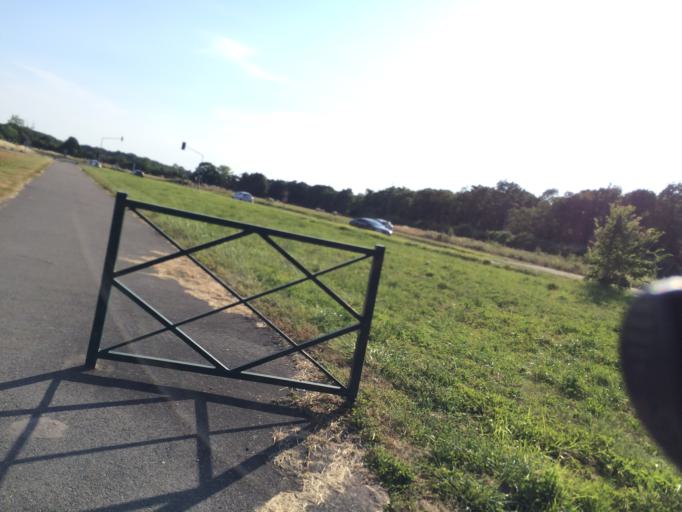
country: FR
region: Ile-de-France
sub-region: Departement de l'Essonne
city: Tigery
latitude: 48.6570
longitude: 2.5127
